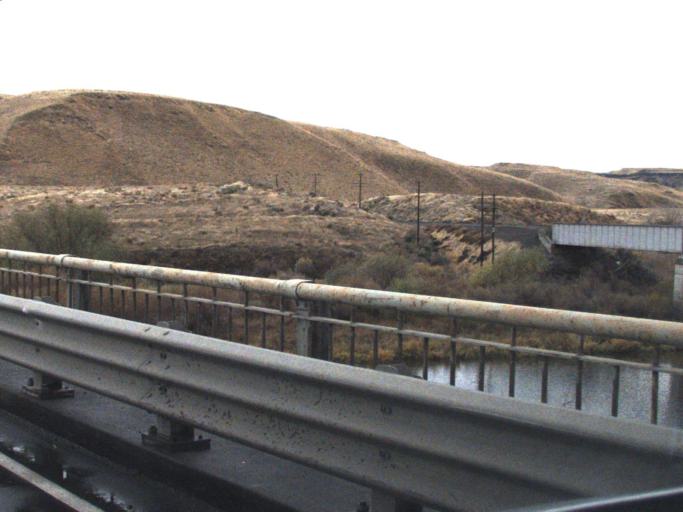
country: US
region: Washington
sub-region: Benton County
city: Finley
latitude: 46.0608
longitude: -118.9094
